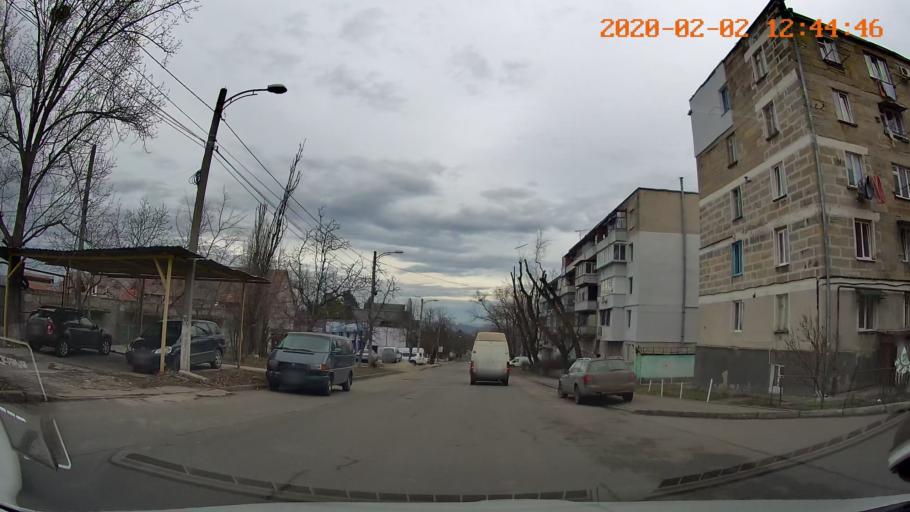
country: MD
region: Chisinau
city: Chisinau
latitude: 47.0036
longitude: 28.8093
